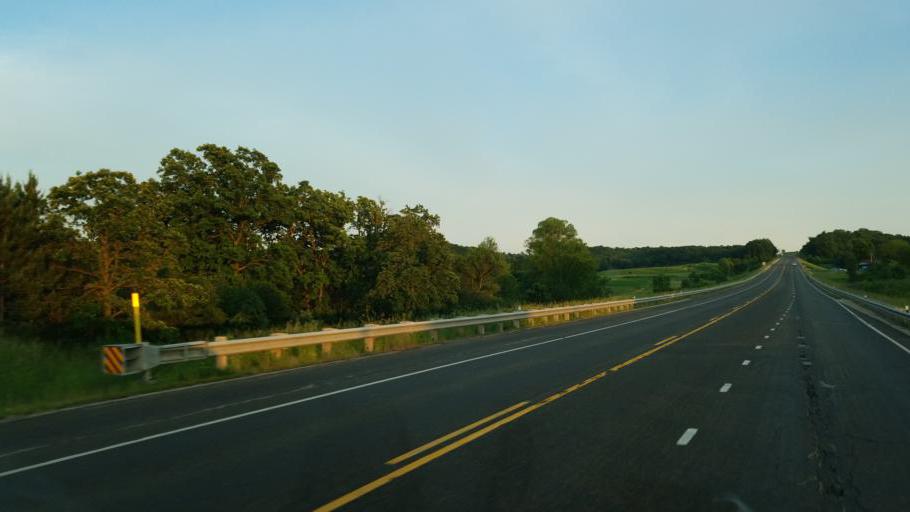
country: US
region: Wisconsin
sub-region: Monroe County
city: Tomah
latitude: 43.9149
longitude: -90.4946
